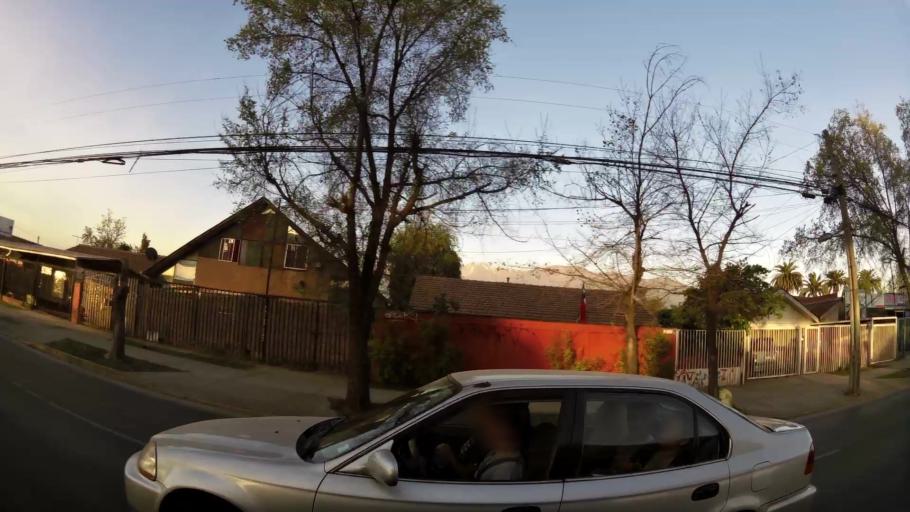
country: CL
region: Santiago Metropolitan
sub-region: Provincia de Santiago
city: La Pintana
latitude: -33.5429
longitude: -70.5894
